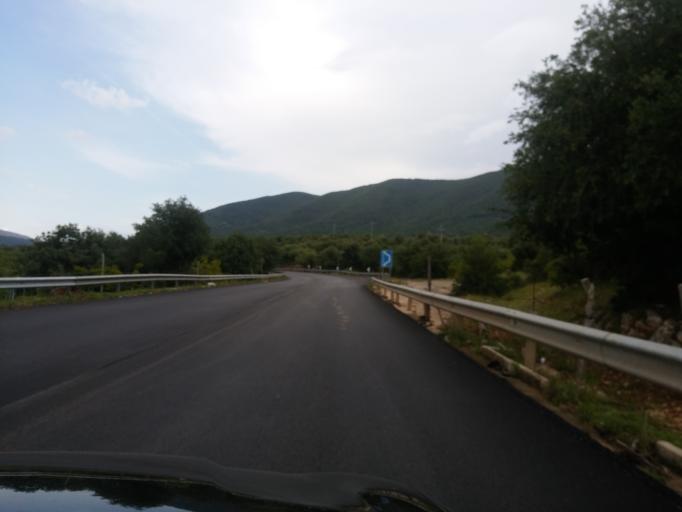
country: IT
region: Apulia
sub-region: Provincia di Foggia
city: Rignano Garganico
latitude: 41.7145
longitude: 15.5445
